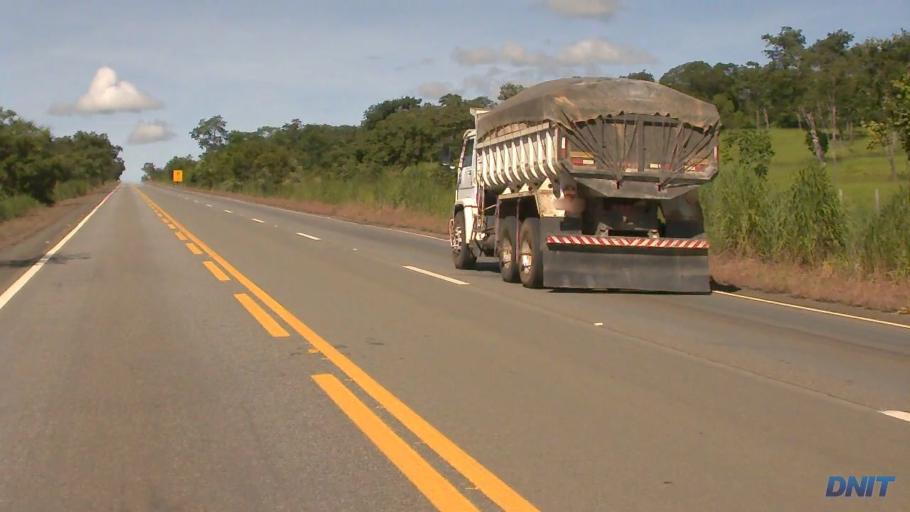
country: BR
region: Goias
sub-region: Padre Bernardo
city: Padre Bernardo
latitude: -15.2063
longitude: -48.4651
